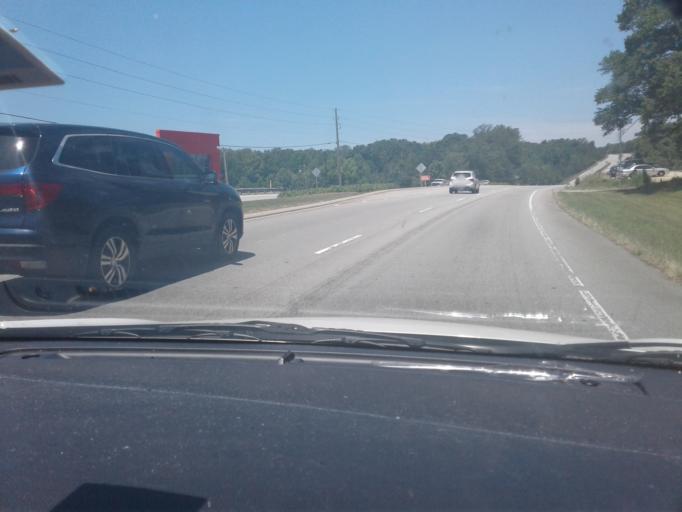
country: US
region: North Carolina
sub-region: Wake County
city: Fuquay-Varina
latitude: 35.6179
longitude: -78.8144
